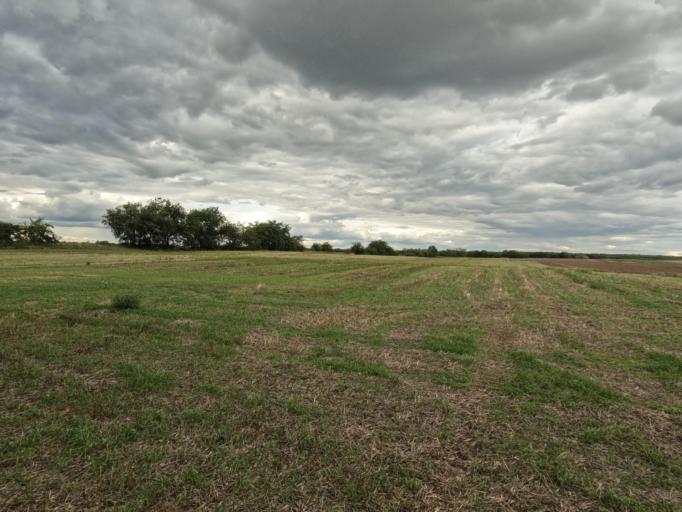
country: HU
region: Tolna
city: Tengelic
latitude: 46.5225
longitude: 18.6752
